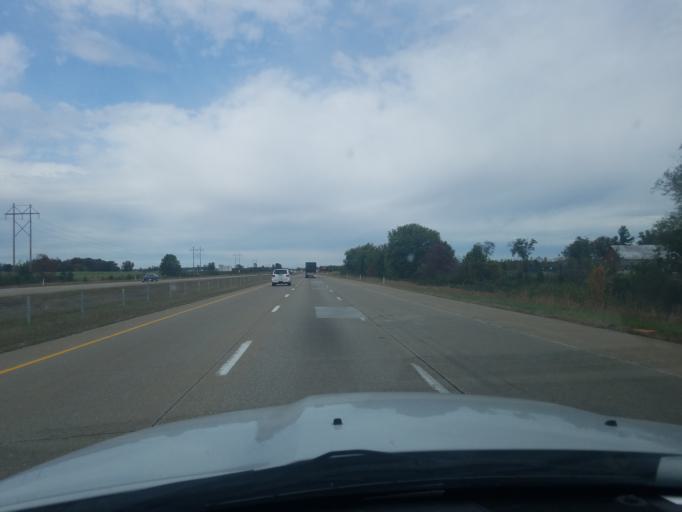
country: US
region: Indiana
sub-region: Vanderburgh County
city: Melody Hill
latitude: 38.0933
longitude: -87.4761
